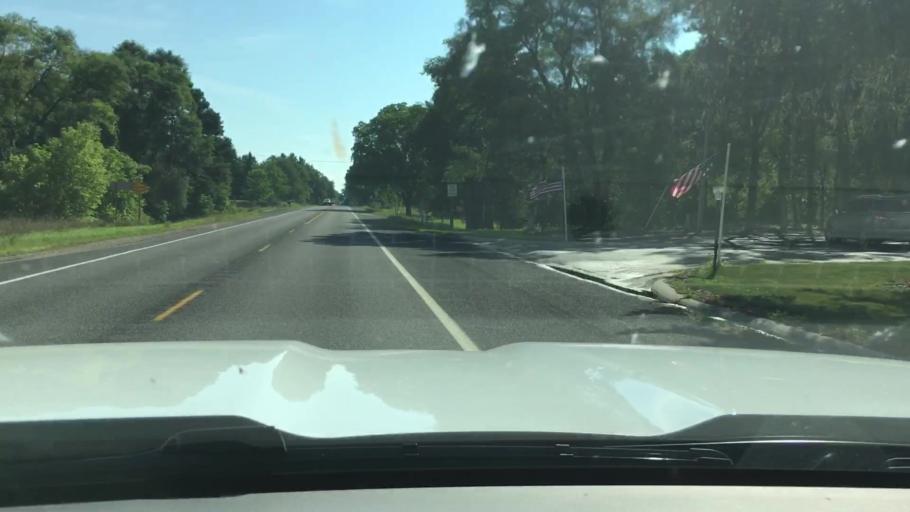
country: US
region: Michigan
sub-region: Montcalm County
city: Edmore
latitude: 43.4083
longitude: -84.8640
